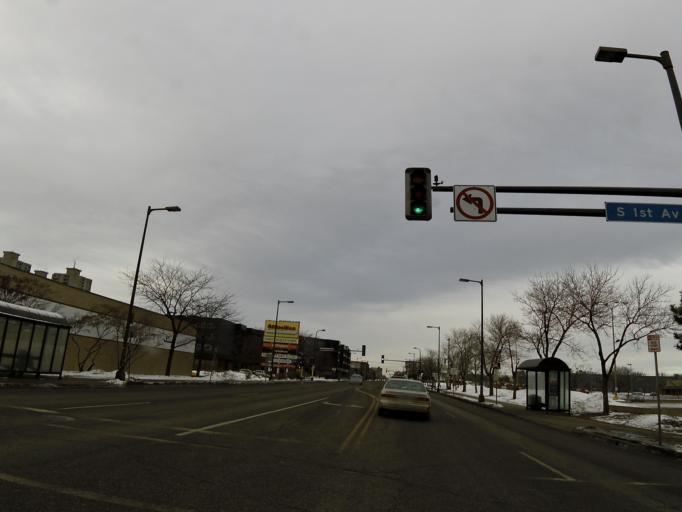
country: US
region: Minnesota
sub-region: Hennepin County
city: Minneapolis
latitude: 44.9484
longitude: -93.2766
